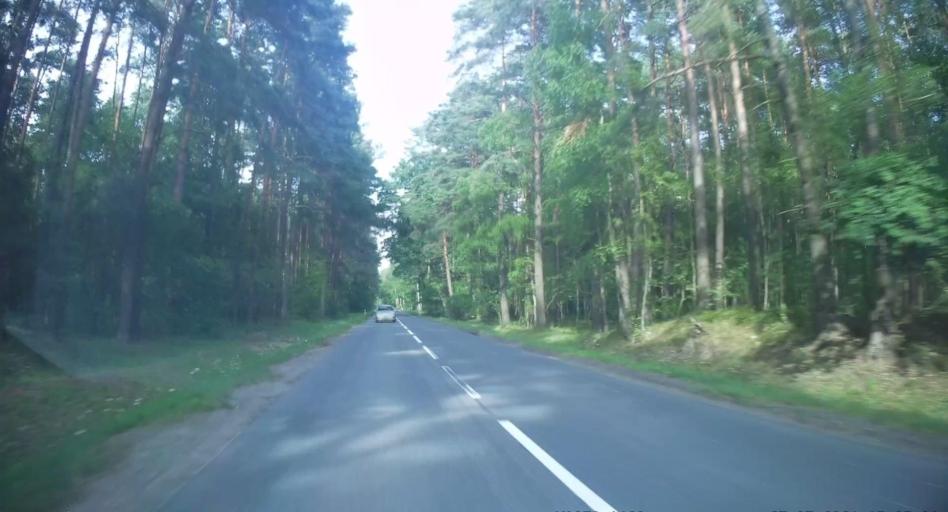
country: PL
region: Lodz Voivodeship
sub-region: Powiat tomaszowski
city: Inowlodz
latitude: 51.5469
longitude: 20.2389
